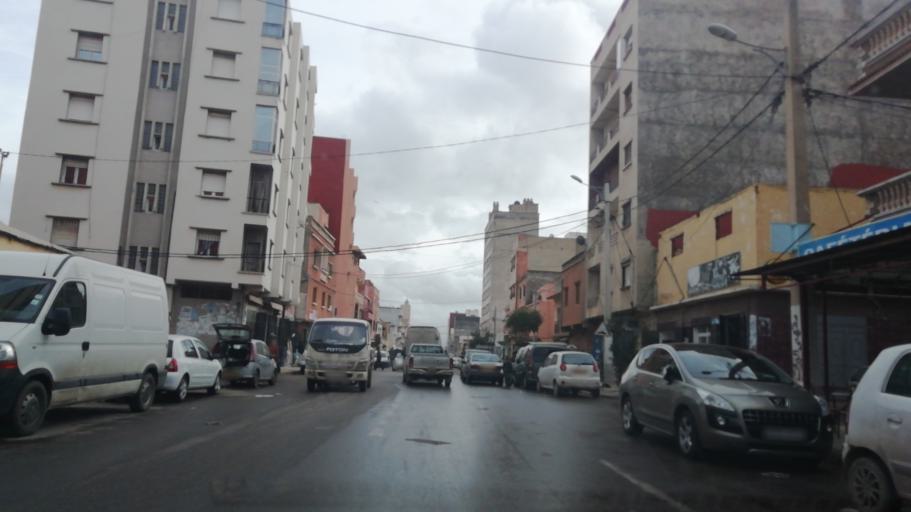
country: DZ
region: Oran
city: Oran
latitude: 35.6865
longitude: -0.6437
